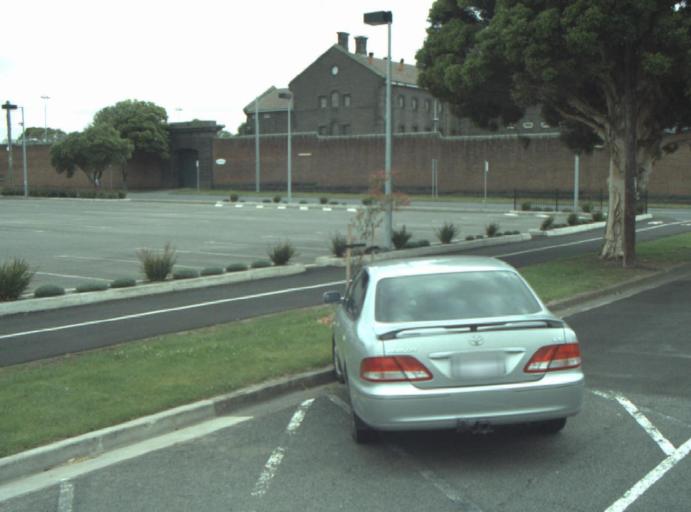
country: AU
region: Victoria
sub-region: Greater Geelong
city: East Geelong
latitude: -38.1550
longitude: 144.3657
